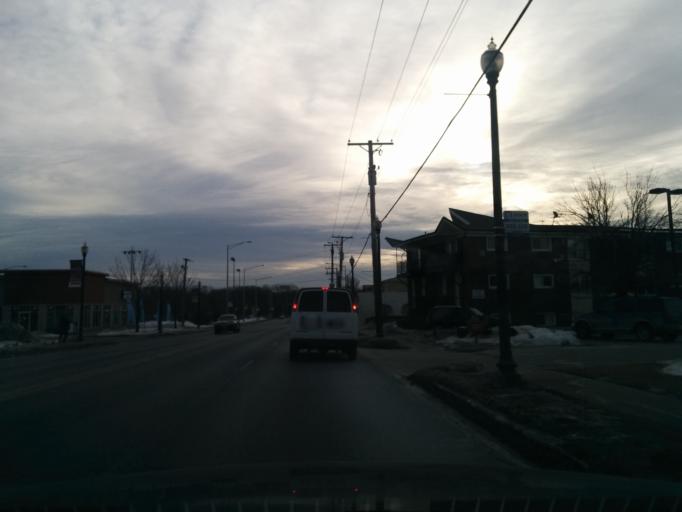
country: US
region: Illinois
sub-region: Cook County
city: Schiller Park
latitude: 41.9540
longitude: -87.8602
